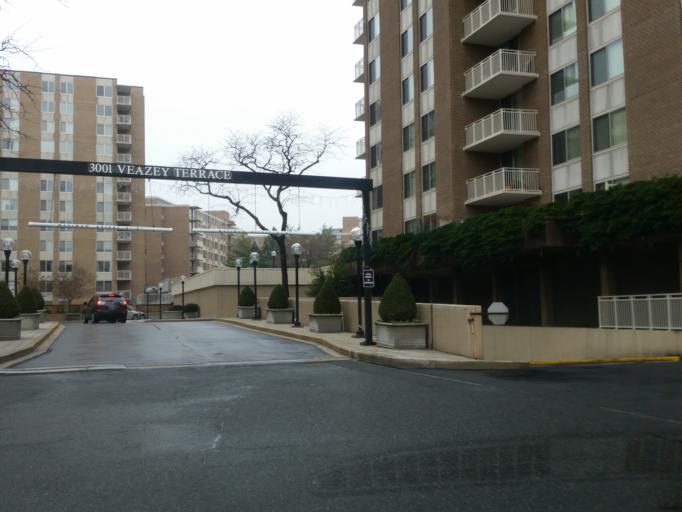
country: US
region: Maryland
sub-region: Montgomery County
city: Chevy Chase Village
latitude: 38.9443
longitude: -77.0624
